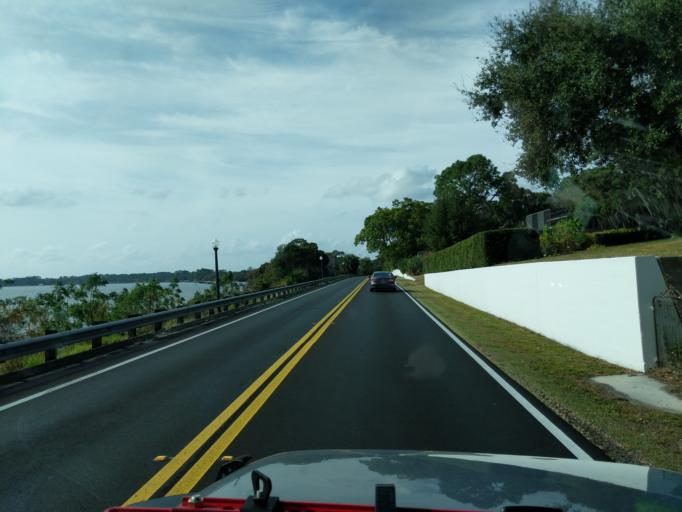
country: US
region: Florida
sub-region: Lake County
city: Mount Dora
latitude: 28.8044
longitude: -81.6526
